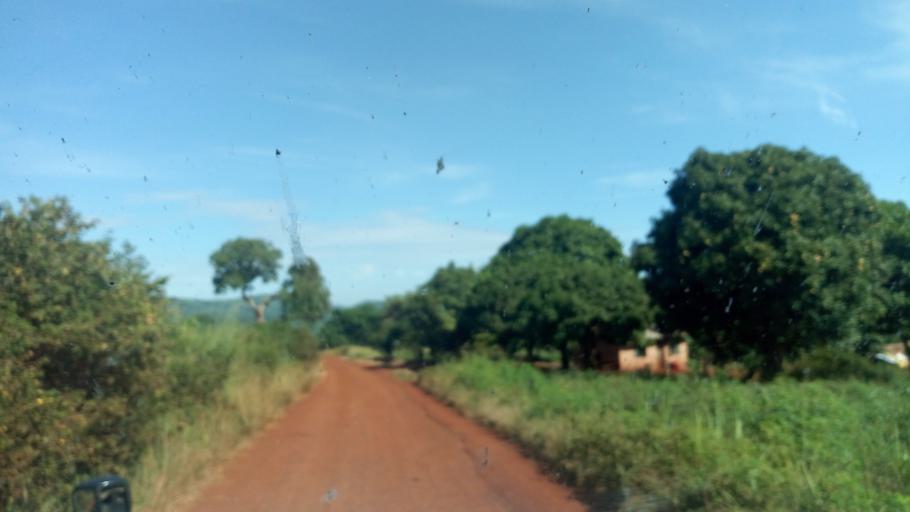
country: UG
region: Western Region
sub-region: Masindi District
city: Masindi
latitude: 1.6432
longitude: 31.7676
